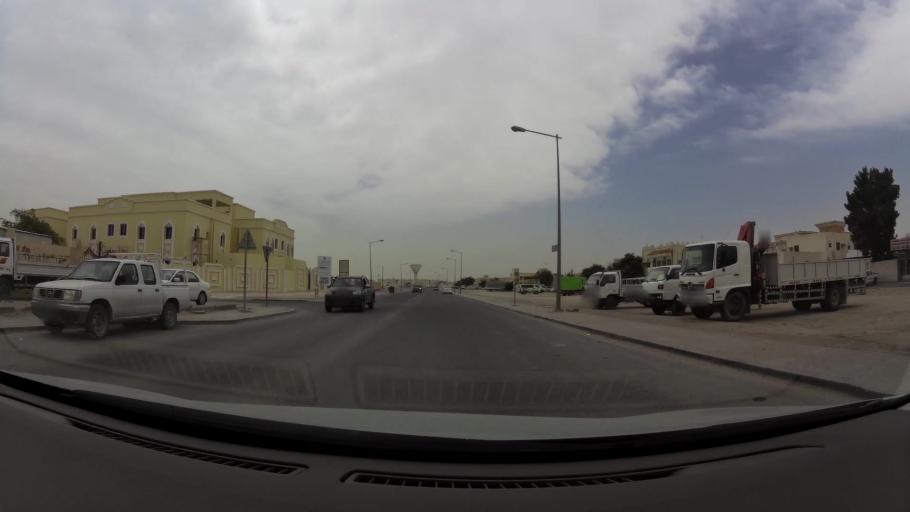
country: QA
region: Baladiyat ar Rayyan
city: Ar Rayyan
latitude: 25.2896
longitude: 51.4590
